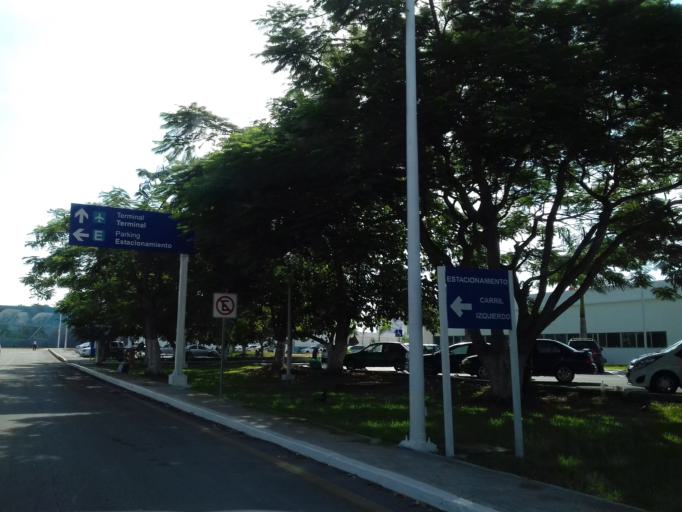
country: MX
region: Yucatan
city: Itzincab Palomeque
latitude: 20.9330
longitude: -89.6647
